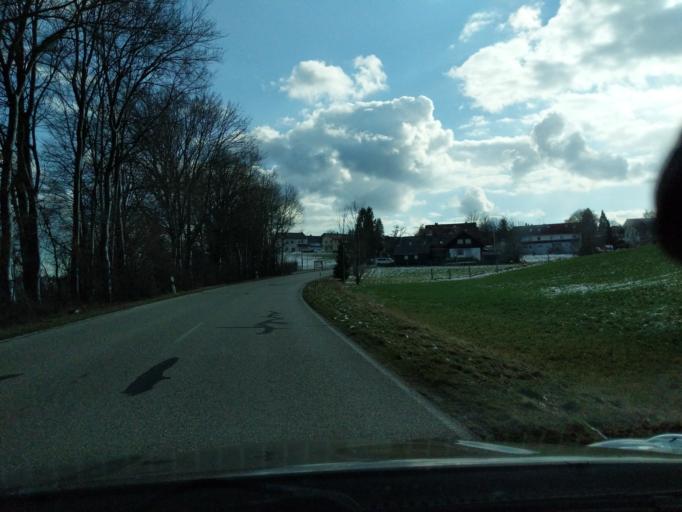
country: DE
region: Bavaria
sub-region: Upper Bavaria
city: Zorneding
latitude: 48.0983
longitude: 11.8336
